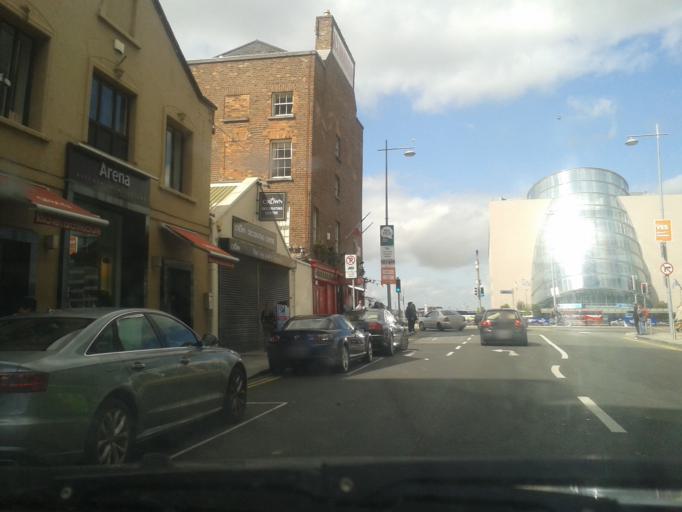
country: IE
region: Leinster
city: Ringsend
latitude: 53.3455
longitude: -6.2404
